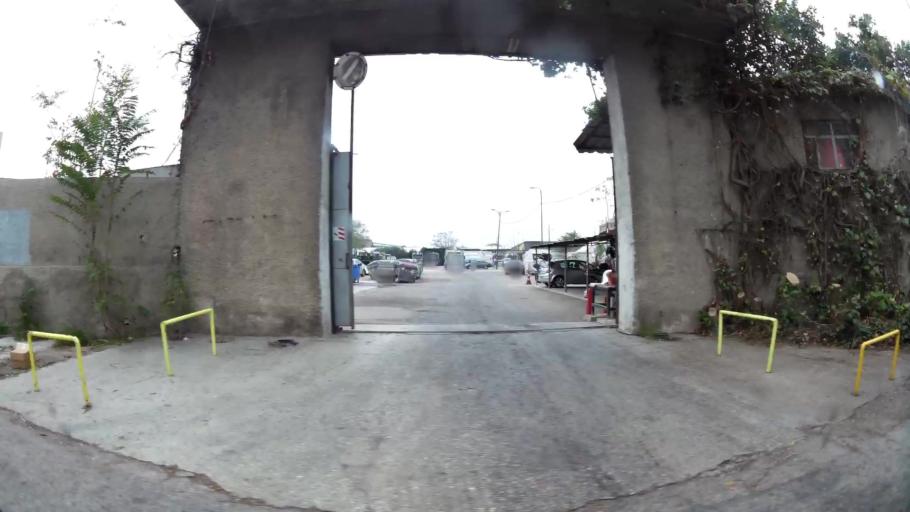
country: GR
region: Attica
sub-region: Nomarchia Athinas
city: Tavros
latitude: 37.9824
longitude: 23.7002
